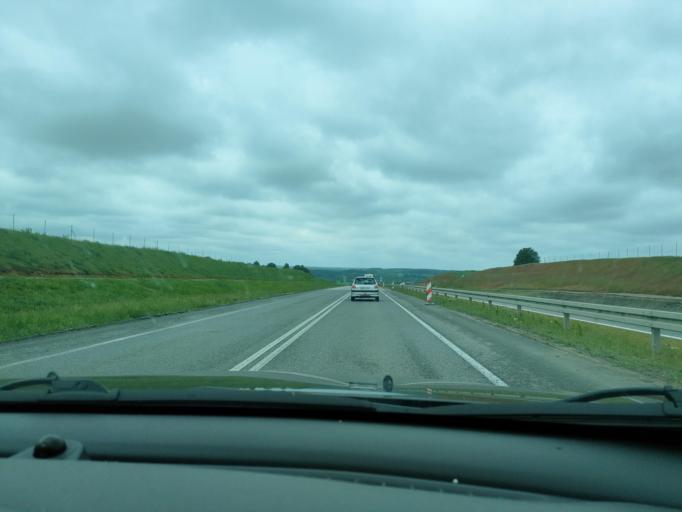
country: PL
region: Kujawsko-Pomorskie
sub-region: Powiat swiecki
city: Swiecie
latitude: 53.4174
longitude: 18.4140
